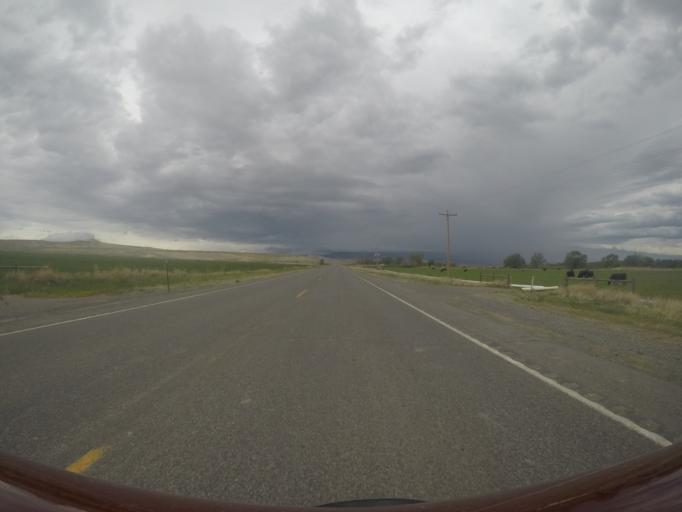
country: US
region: Wyoming
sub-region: Big Horn County
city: Lovell
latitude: 44.8701
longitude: -108.3201
